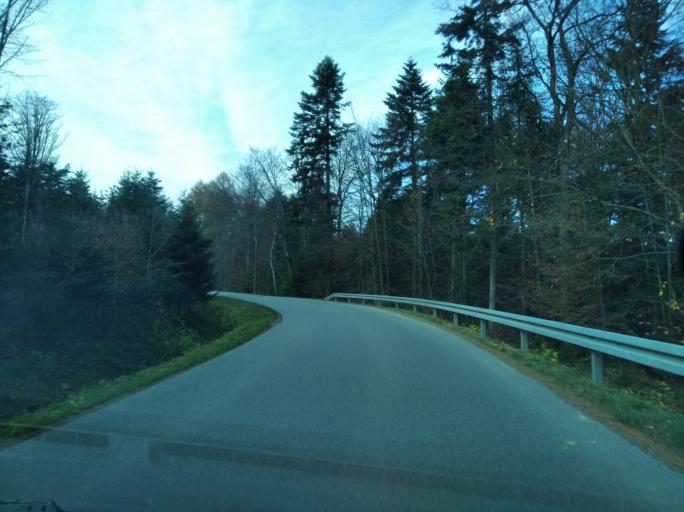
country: PL
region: Subcarpathian Voivodeship
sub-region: Powiat ropczycko-sedziszowski
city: Zagorzyce
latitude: 49.9608
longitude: 21.6928
